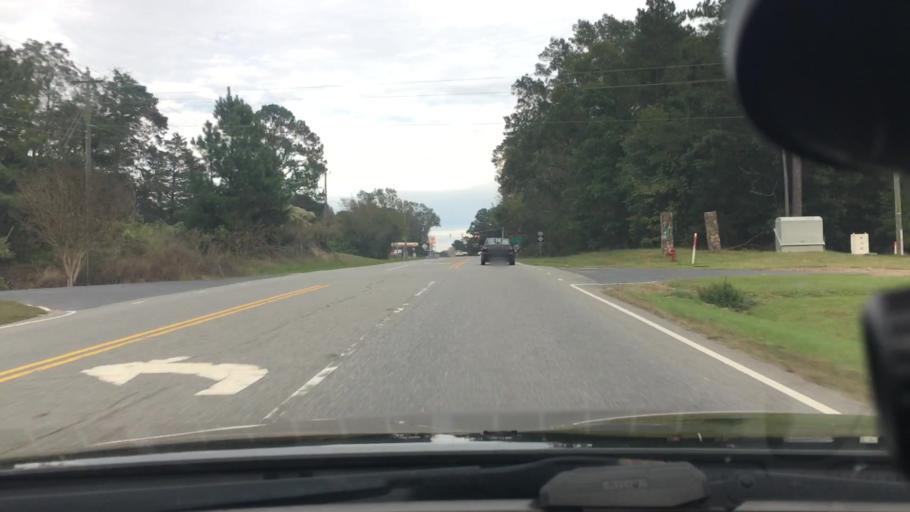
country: US
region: North Carolina
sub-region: Moore County
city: Robbins
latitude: 35.4043
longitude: -79.5778
